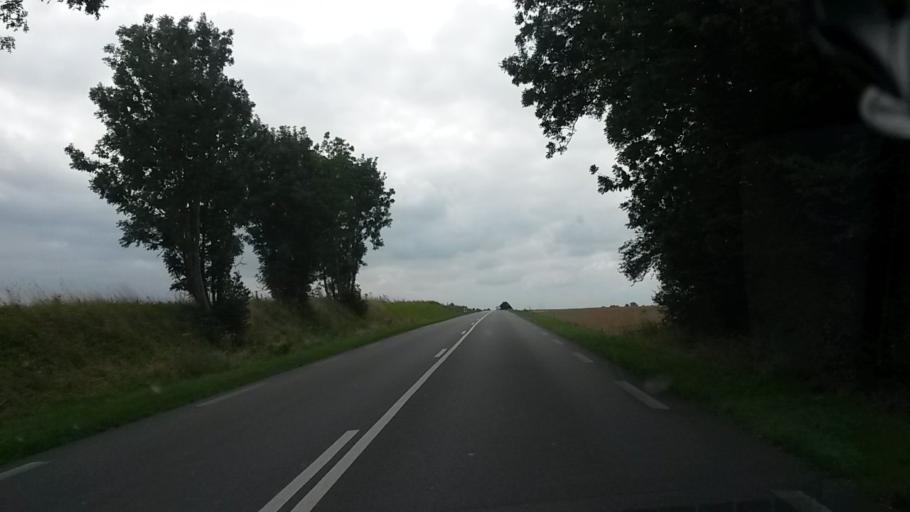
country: FR
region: Picardie
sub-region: Departement de la Somme
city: Corbie
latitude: 49.9681
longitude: 2.5330
